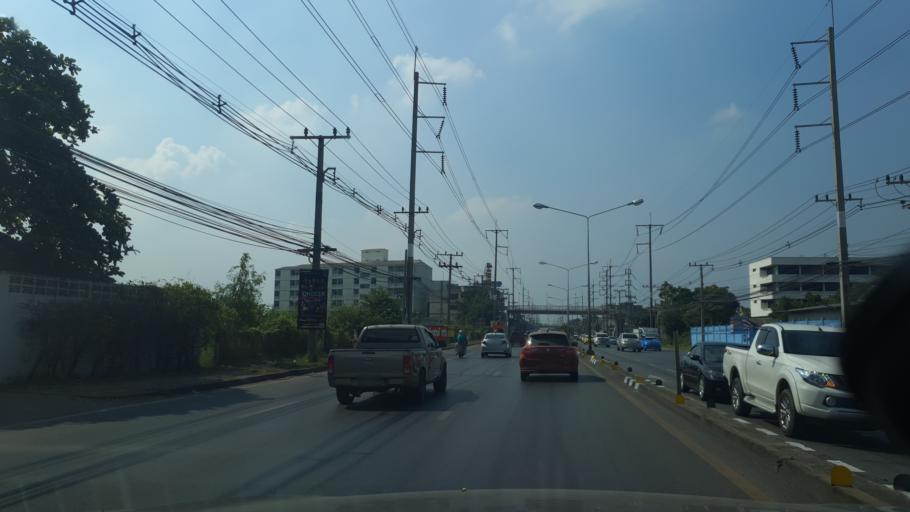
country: TH
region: Samut Sakhon
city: Krathum Baen
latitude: 13.6681
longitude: 100.2791
